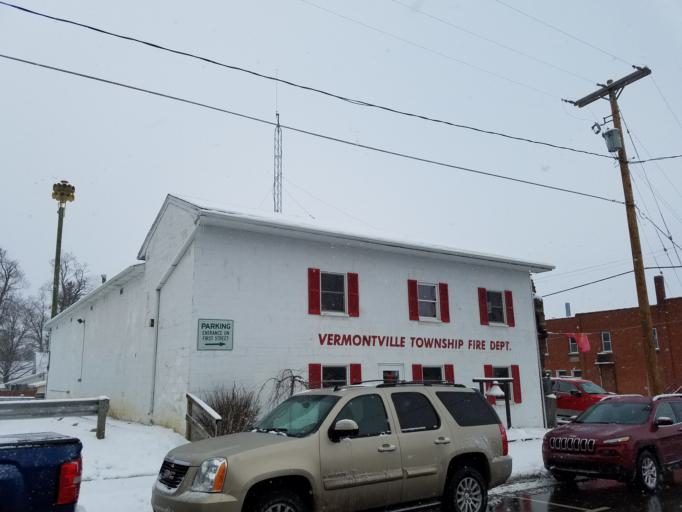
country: US
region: Michigan
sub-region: Barry County
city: Nashville
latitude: 42.6271
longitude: -85.0248
